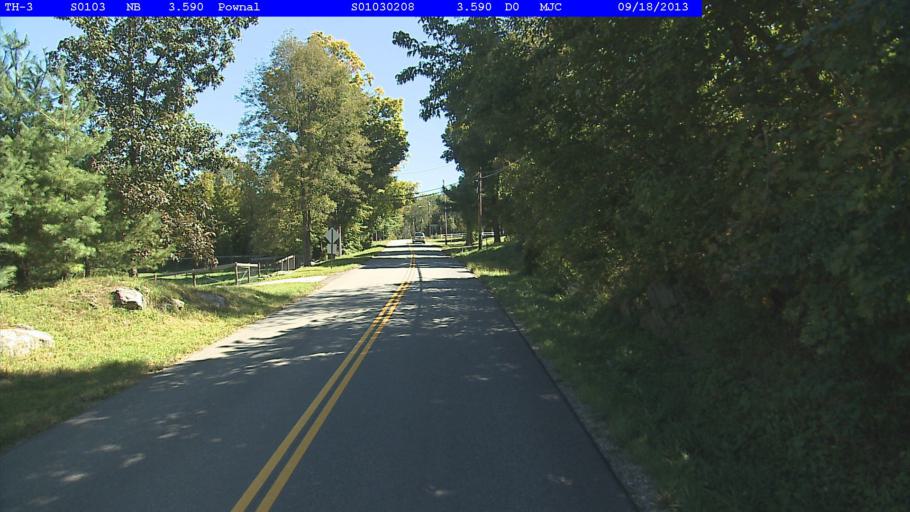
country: US
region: Vermont
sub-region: Bennington County
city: Bennington
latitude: 42.7963
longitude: -73.2096
